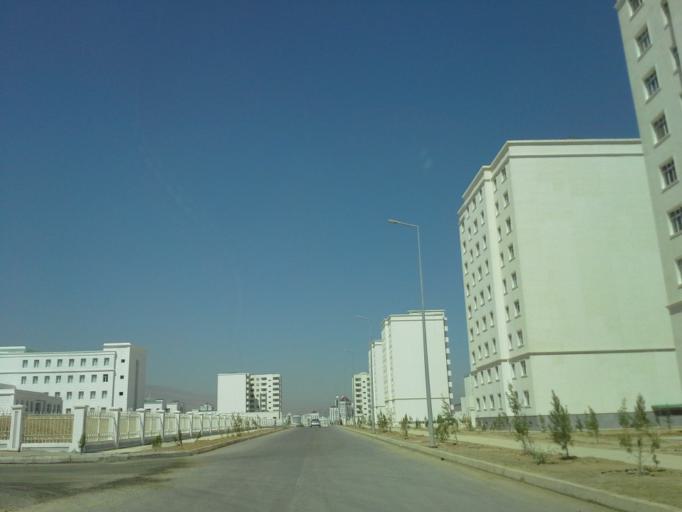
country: TM
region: Ahal
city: Ashgabat
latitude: 37.8935
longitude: 58.4114
